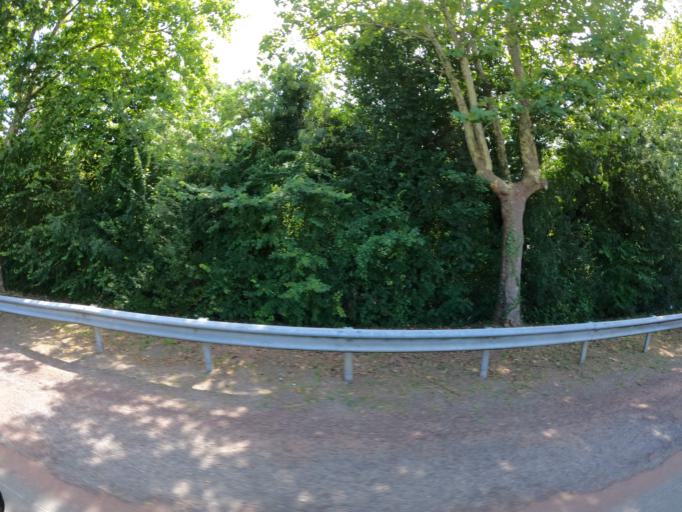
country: FR
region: Poitou-Charentes
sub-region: Departement des Deux-Sevres
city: Bessines
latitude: 46.3002
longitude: -0.4954
